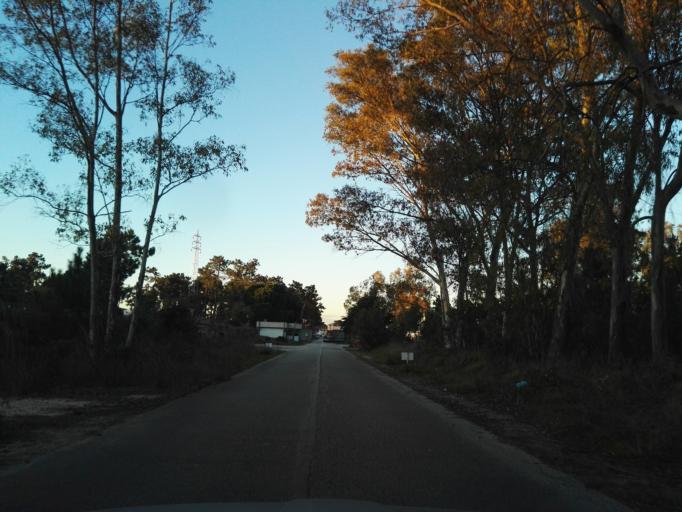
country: PT
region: Setubal
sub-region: Seixal
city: Corroios
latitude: 38.6242
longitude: -9.1458
